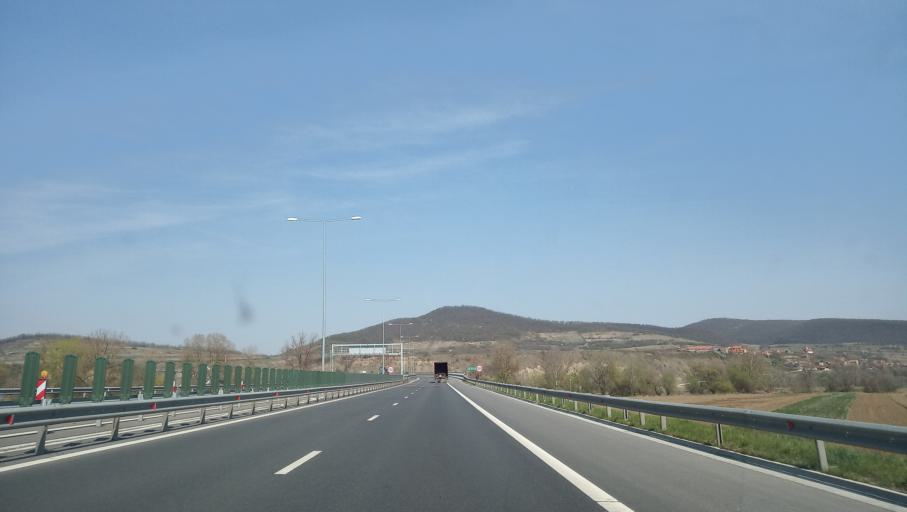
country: RO
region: Alba
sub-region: Municipiul Aiud
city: Aiud
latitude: 46.3346
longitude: 23.7309
